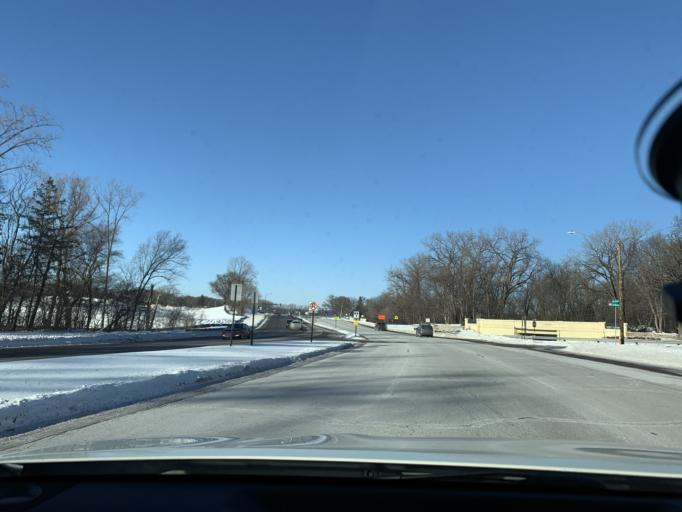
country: US
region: Minnesota
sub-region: Anoka County
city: Coon Rapids
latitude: 45.1506
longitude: -93.2960
